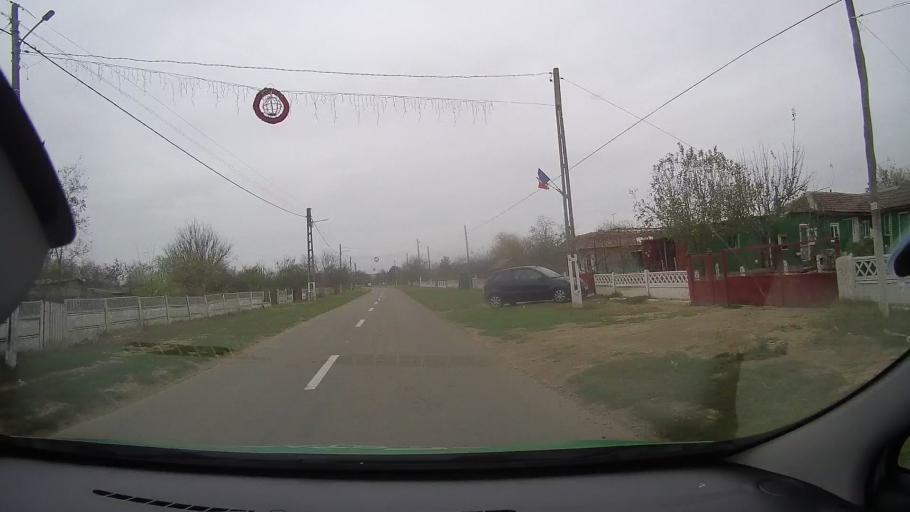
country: RO
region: Constanta
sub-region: Comuna Saraiu
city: Saraiu
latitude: 44.7210
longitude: 28.1623
